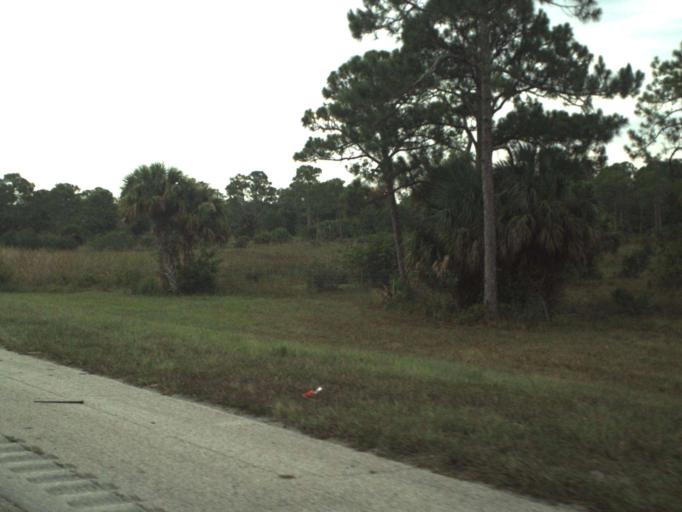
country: US
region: Florida
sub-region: Martin County
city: Palm City
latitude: 27.1267
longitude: -80.3235
